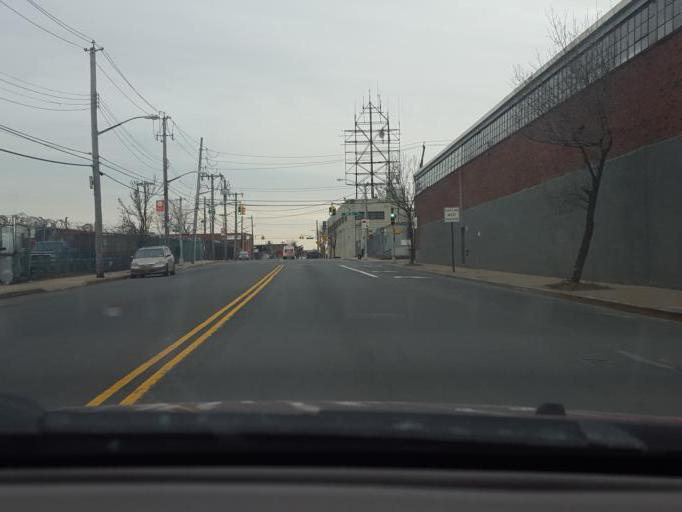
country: US
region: New York
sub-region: Queens County
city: Long Island City
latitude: 40.7285
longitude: -73.9121
